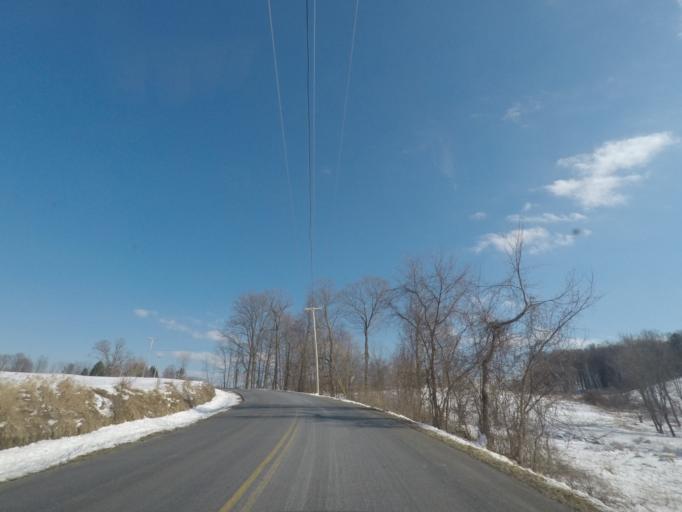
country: US
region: New York
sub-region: Rensselaer County
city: Hoosick Falls
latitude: 42.8714
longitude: -73.4970
